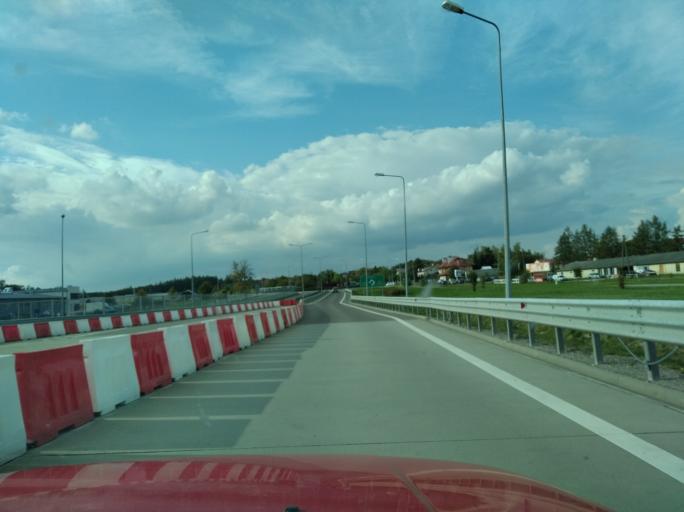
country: PL
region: Subcarpathian Voivodeship
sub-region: Powiat jaroslawski
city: Pawlosiow
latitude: 49.9761
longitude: 22.6438
